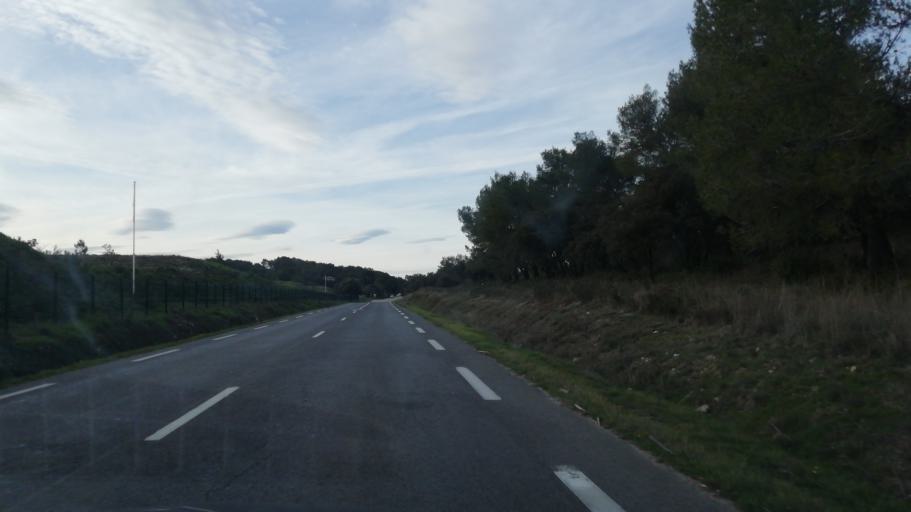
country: FR
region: Languedoc-Roussillon
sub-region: Departement du Gard
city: Caveirac
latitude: 43.8452
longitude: 4.2996
